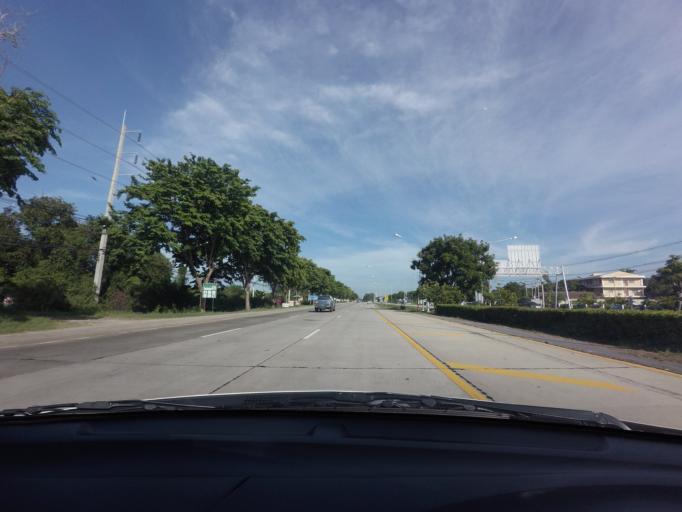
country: TH
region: Suphan Buri
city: Suphan Buri
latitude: 14.4414
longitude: 100.1347
